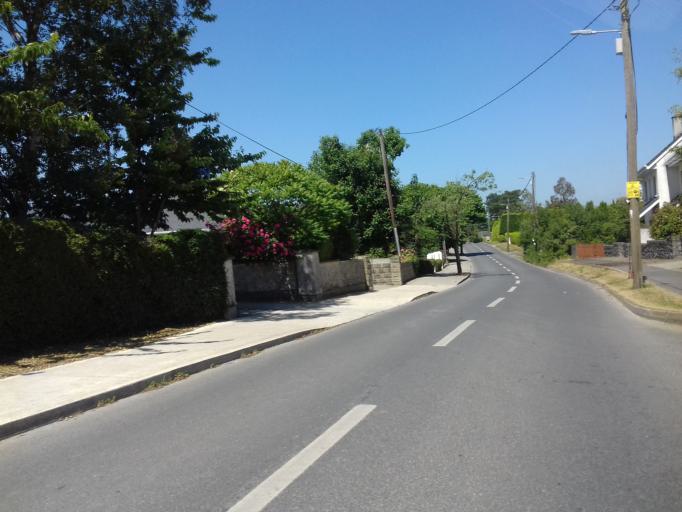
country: IE
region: Leinster
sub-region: An Mhi
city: Ashbourne
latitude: 53.5211
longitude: -6.3158
